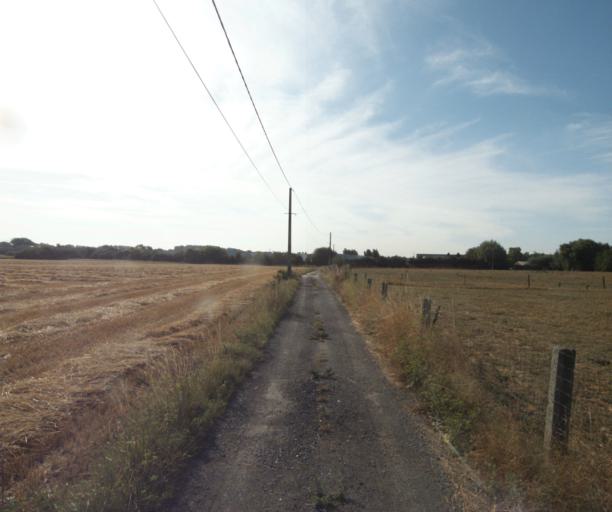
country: FR
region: Nord-Pas-de-Calais
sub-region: Departement du Nord
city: Roncq
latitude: 50.7572
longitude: 3.1305
